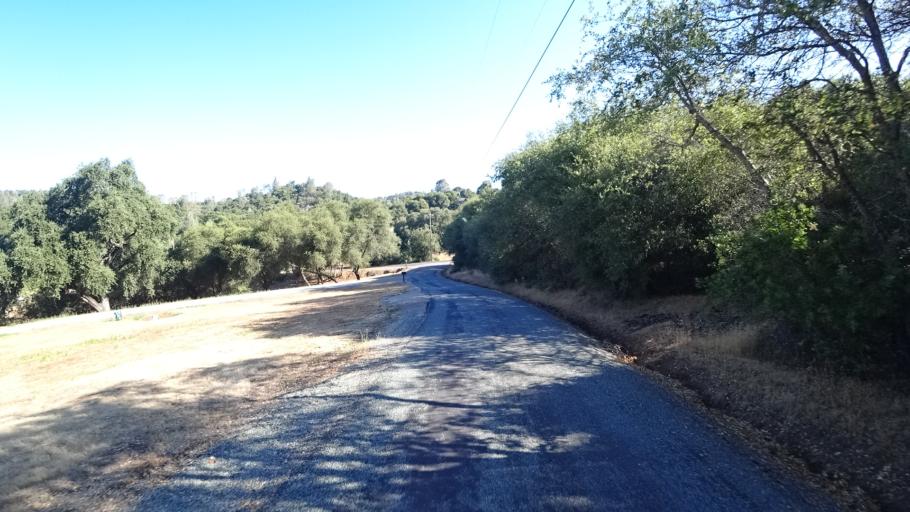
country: US
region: California
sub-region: Calaveras County
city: San Andreas
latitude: 38.2461
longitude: -120.7047
